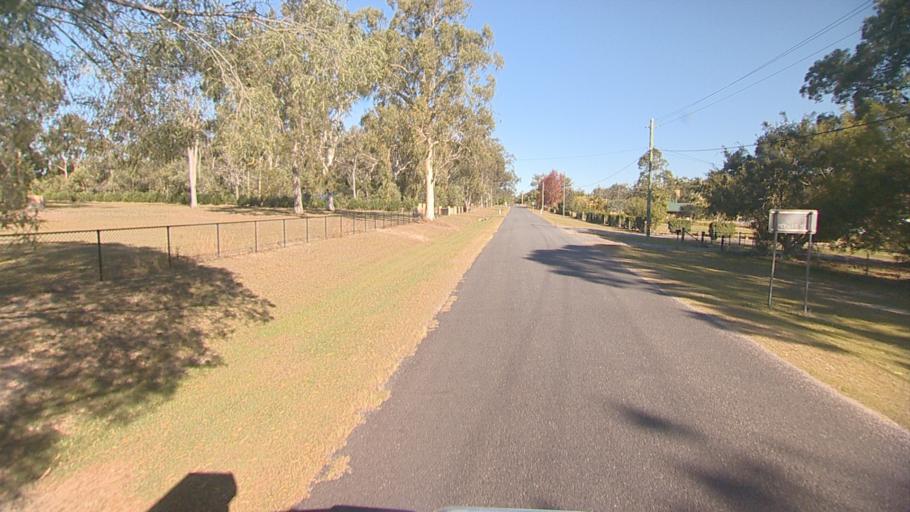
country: AU
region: Queensland
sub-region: Logan
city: Chambers Flat
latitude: -27.7353
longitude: 153.0779
